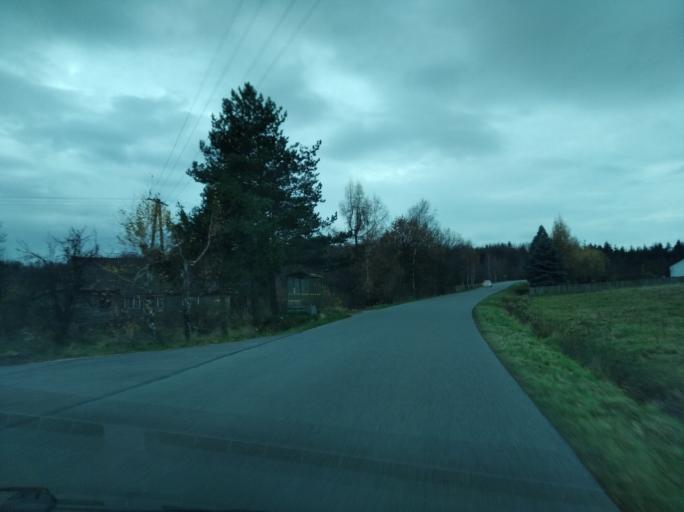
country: PL
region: Subcarpathian Voivodeship
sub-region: Powiat ropczycko-sedziszowski
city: Zagorzyce
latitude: 49.9702
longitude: 21.7010
